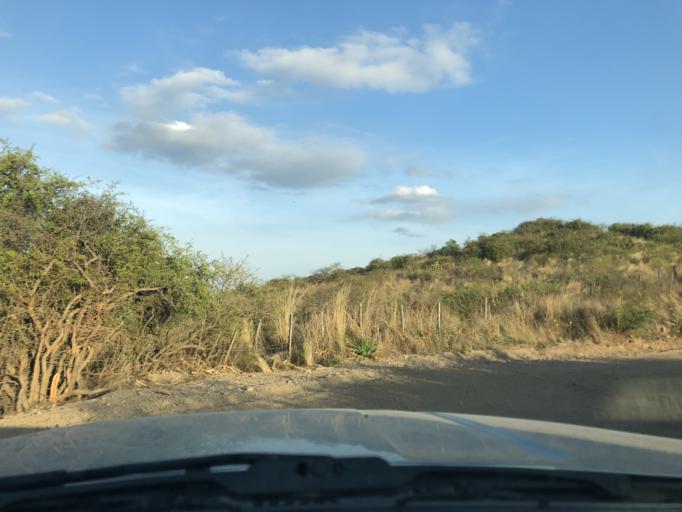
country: AR
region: Cordoba
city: Agua de Oro
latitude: -31.0550
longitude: -64.3509
